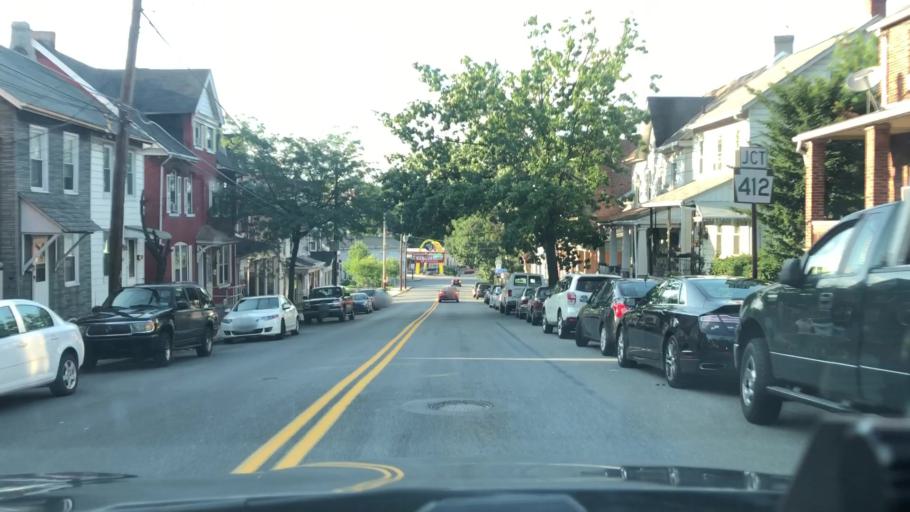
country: US
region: Pennsylvania
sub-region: Lehigh County
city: Fountain Hill
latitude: 40.6070
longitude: -75.3852
